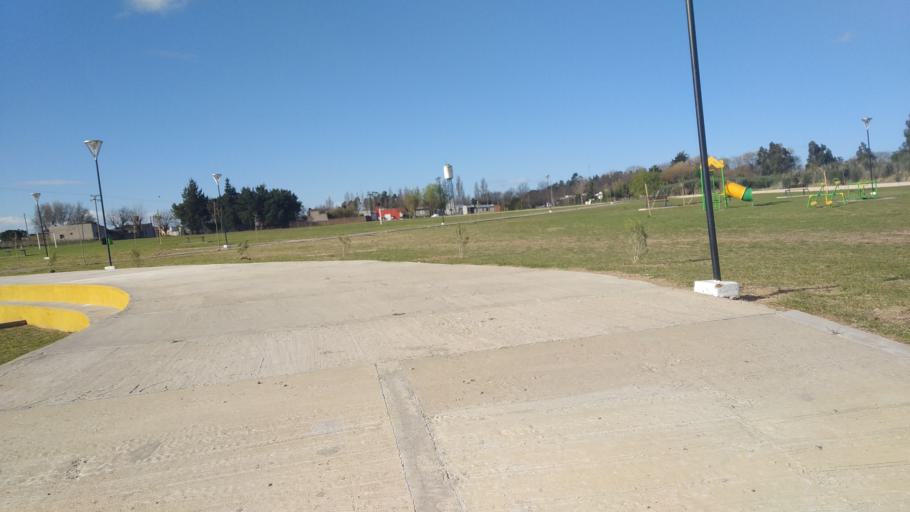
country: AR
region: Buenos Aires
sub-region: Partido de Loberia
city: Loberia
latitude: -38.2025
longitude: -58.7405
